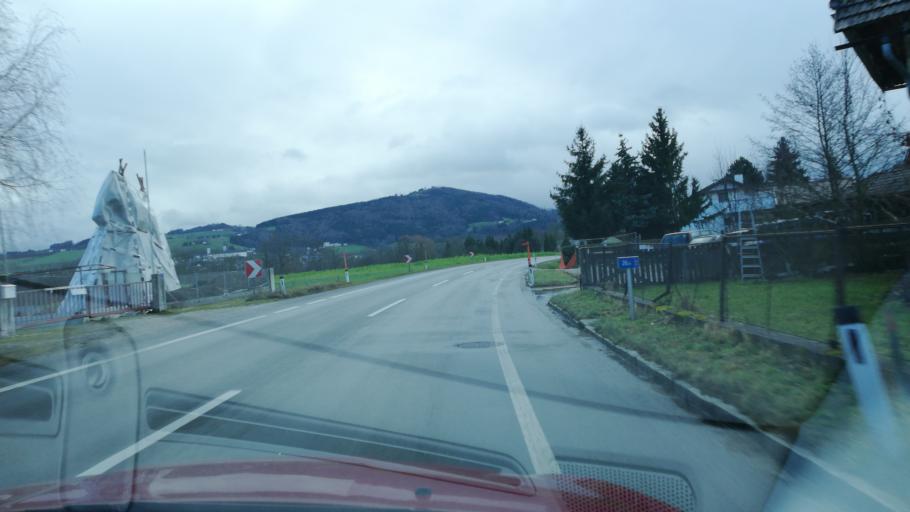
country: AT
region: Upper Austria
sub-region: Politischer Bezirk Kirchdorf an der Krems
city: Micheldorf in Oberoesterreich
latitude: 47.9488
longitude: 14.0973
